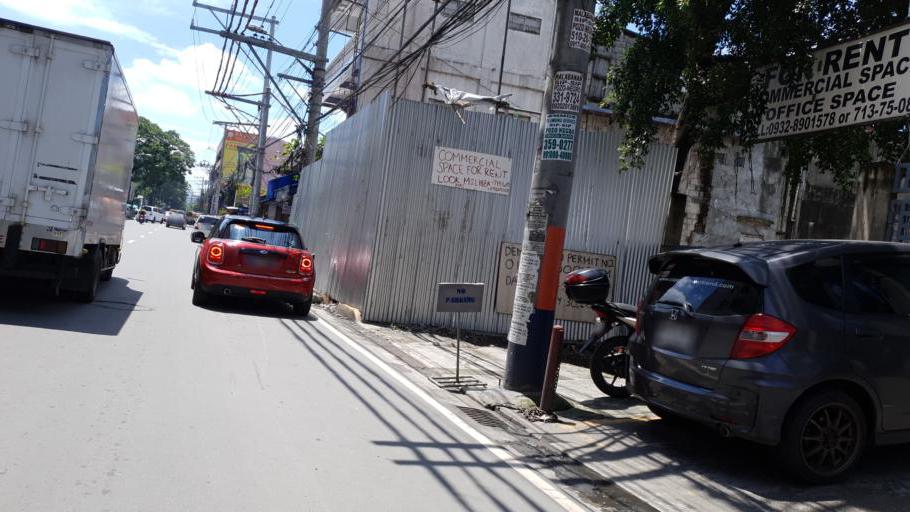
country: PH
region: Metro Manila
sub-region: San Juan
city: San Juan
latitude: 14.5998
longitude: 121.0140
